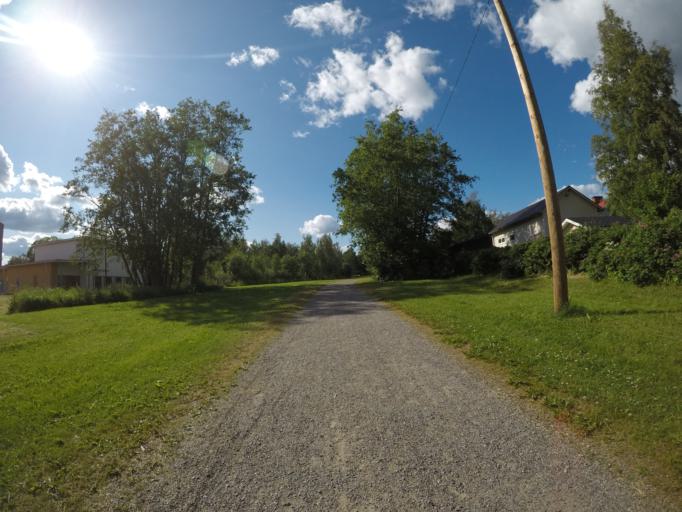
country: FI
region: Haeme
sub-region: Haemeenlinna
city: Haemeenlinna
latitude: 61.0000
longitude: 24.4955
